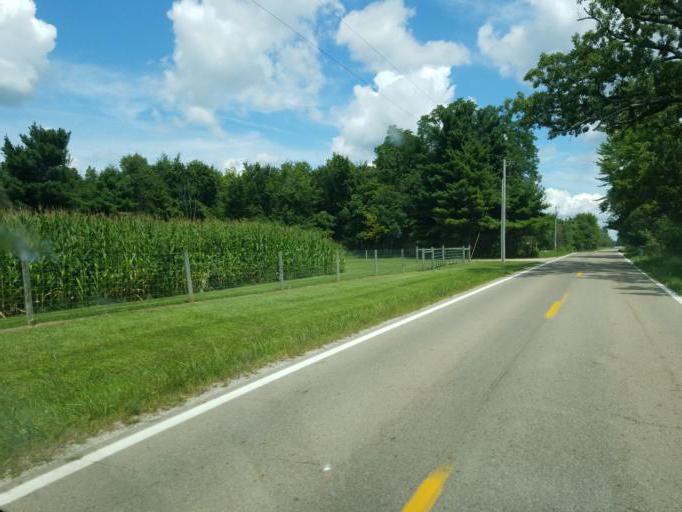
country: US
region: Ohio
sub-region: Knox County
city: Centerburg
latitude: 40.3477
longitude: -82.7814
